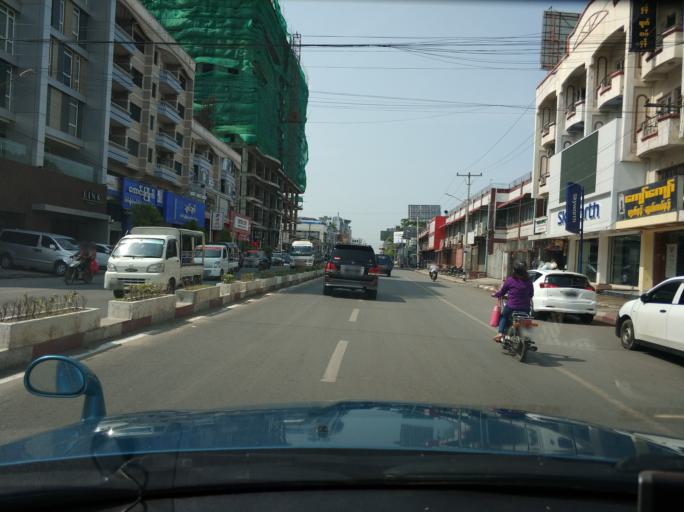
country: MM
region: Mandalay
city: Mandalay
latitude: 21.9754
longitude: 96.0867
